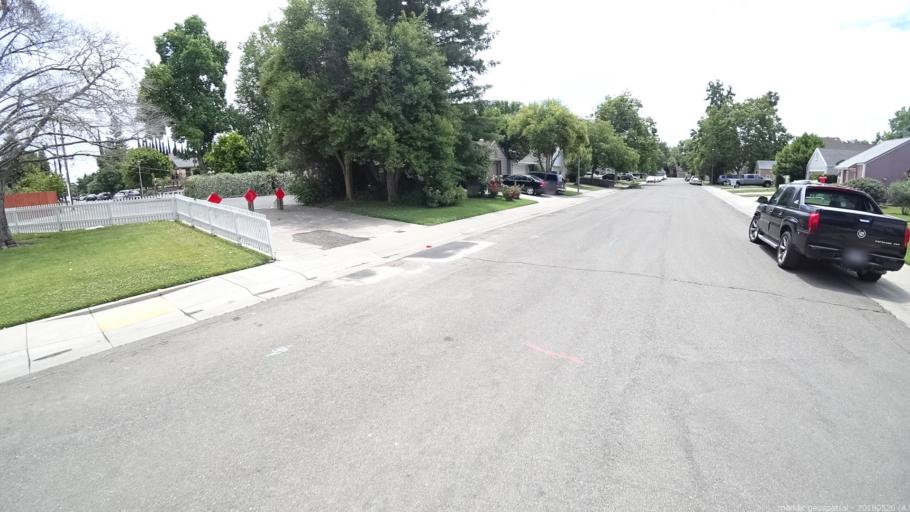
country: US
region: California
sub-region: Sacramento County
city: Sacramento
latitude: 38.6109
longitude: -121.4914
